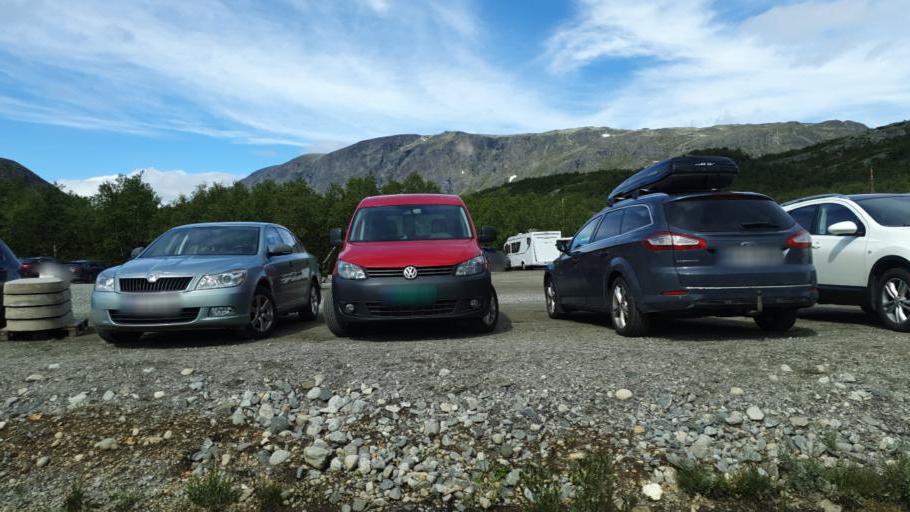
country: NO
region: Oppland
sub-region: Oystre Slidre
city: Heggenes
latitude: 61.4877
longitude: 8.8351
